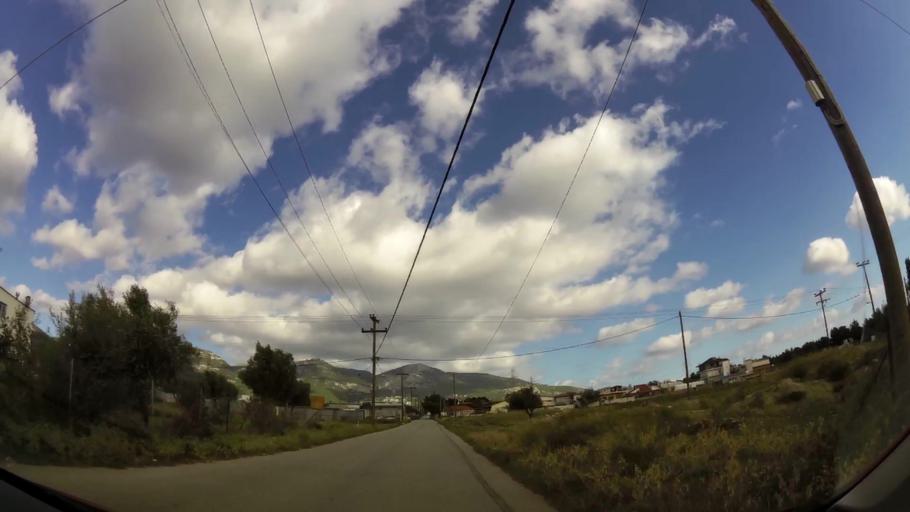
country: GR
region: Attica
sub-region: Nomarchia Anatolikis Attikis
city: Thrakomakedones
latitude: 38.1081
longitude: 23.7576
